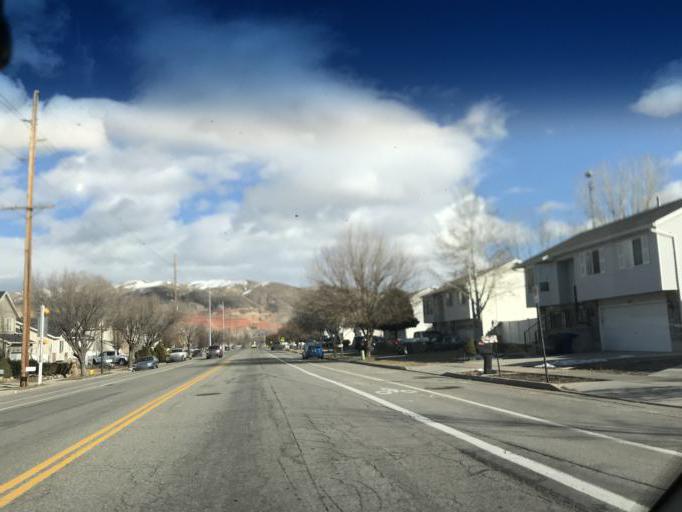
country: US
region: Utah
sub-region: Davis County
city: North Salt Lake
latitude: 40.8057
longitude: -111.9441
